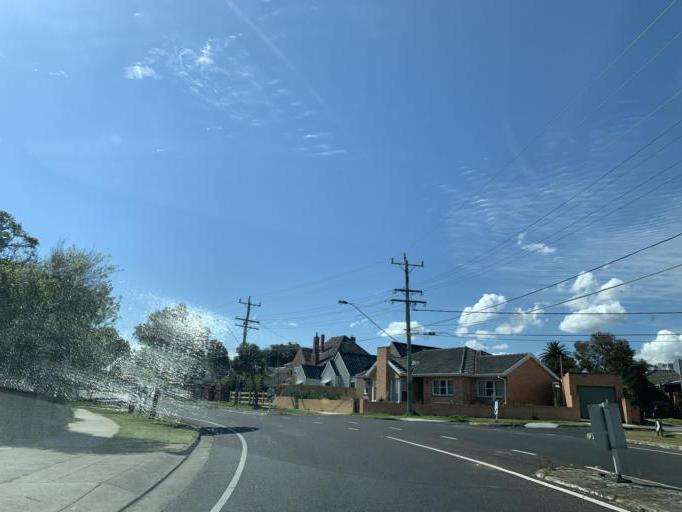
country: AU
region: Victoria
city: Hampton
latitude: -37.9564
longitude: 145.0115
